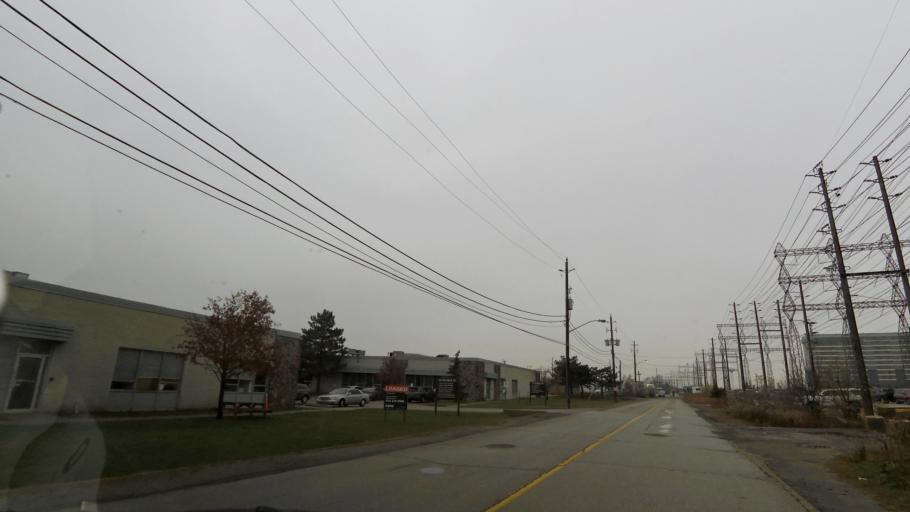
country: CA
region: Ontario
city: Etobicoke
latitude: 43.6867
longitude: -79.5789
